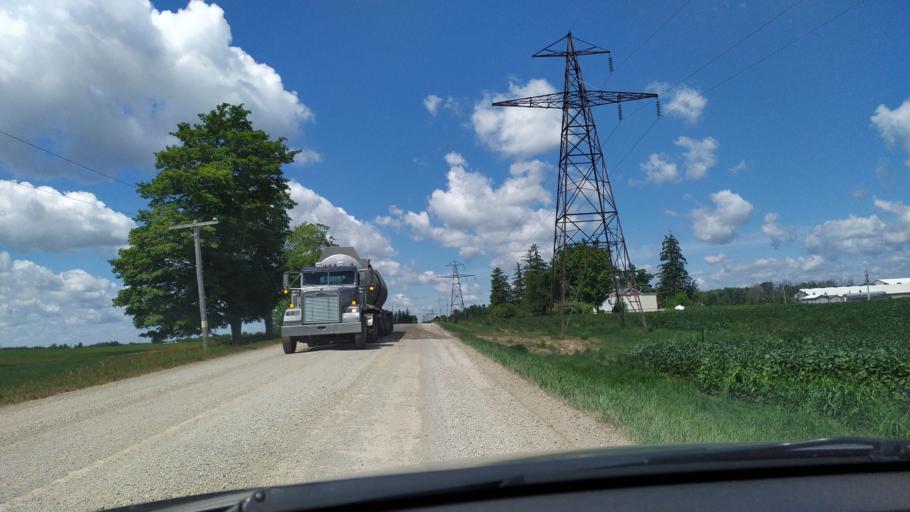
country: CA
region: Ontario
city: Stratford
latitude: 43.3878
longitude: -80.8160
